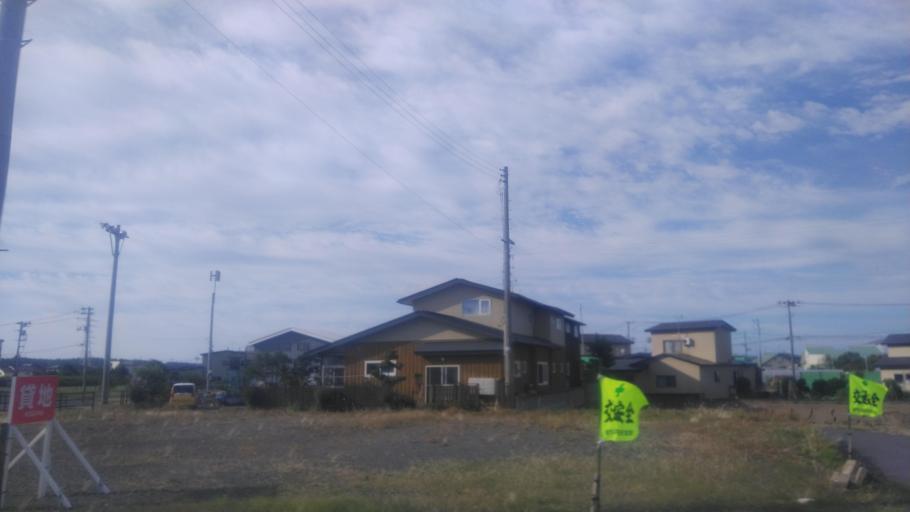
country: JP
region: Akita
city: Noshiromachi
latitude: 40.1889
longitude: 140.0400
